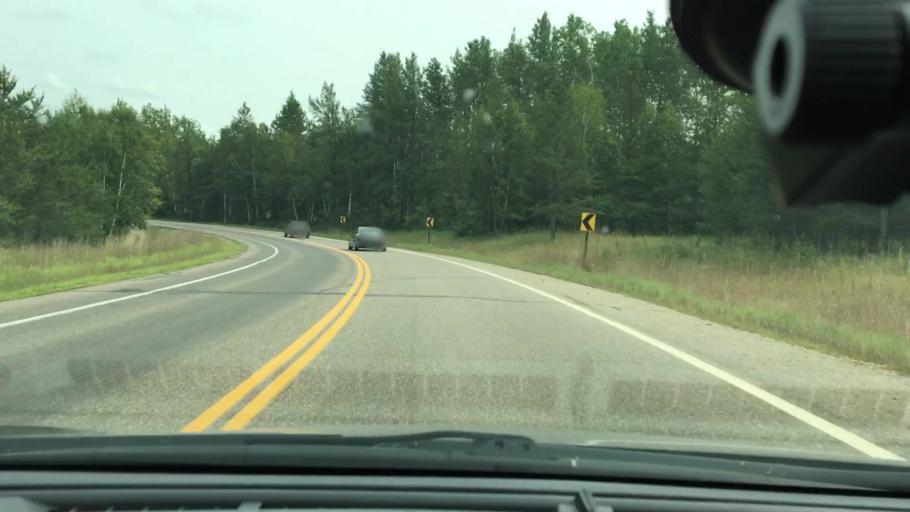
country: US
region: Minnesota
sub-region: Crow Wing County
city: Cross Lake
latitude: 46.7317
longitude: -94.0286
